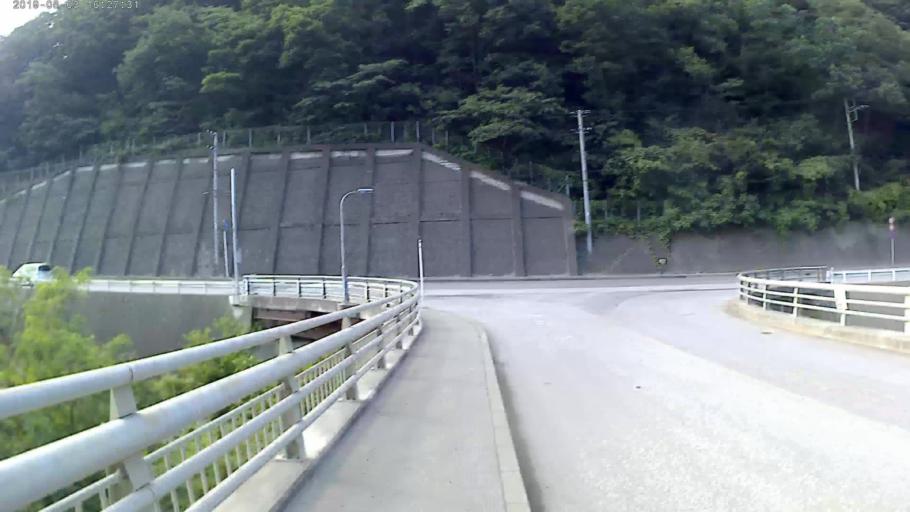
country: JP
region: Yamanashi
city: Otsuki
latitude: 35.6006
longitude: 138.8979
